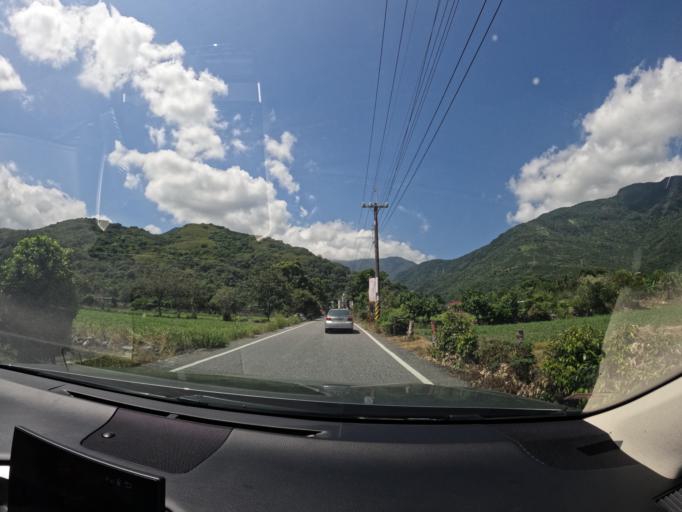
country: TW
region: Taiwan
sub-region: Hualien
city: Hualian
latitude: 23.7143
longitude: 121.4140
